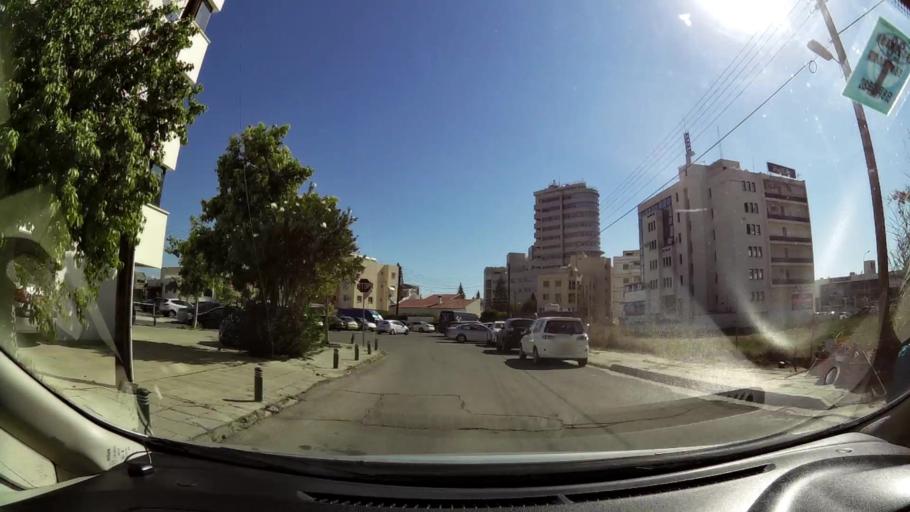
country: CY
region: Larnaka
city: Larnaca
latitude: 34.9312
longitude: 33.6293
